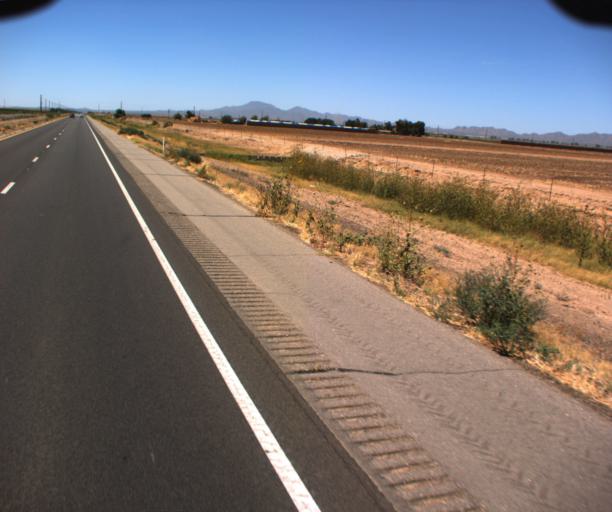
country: US
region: Arizona
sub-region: Pinal County
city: Maricopa
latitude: 32.9921
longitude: -112.0481
